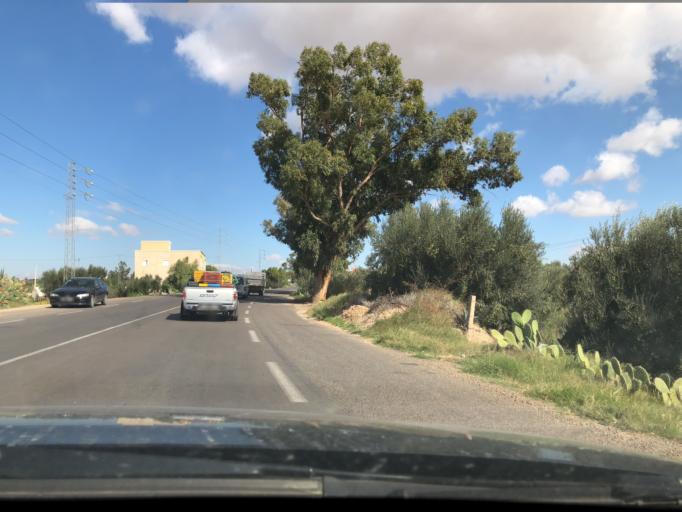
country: TN
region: Al Qasrayn
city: Kasserine
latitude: 35.2048
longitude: 8.8812
